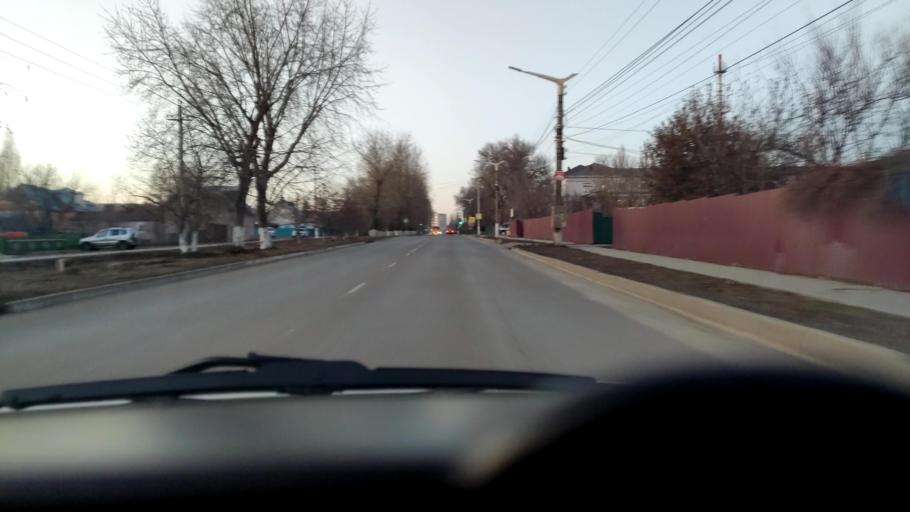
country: RU
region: Voronezj
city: Semiluki
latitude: 51.6938
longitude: 39.0327
